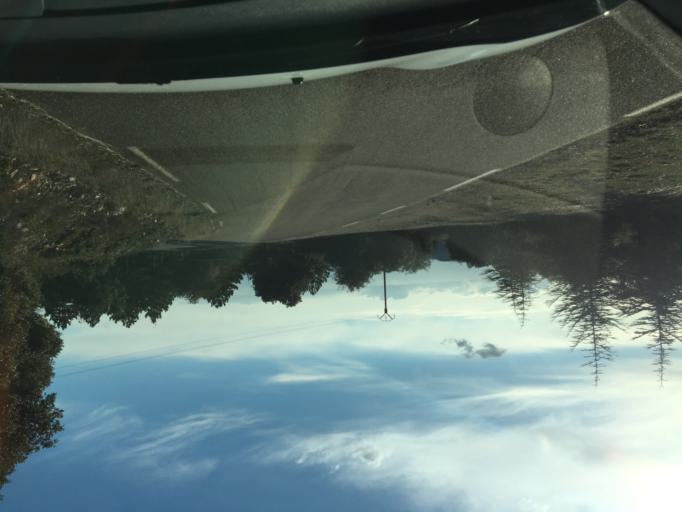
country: FR
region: Provence-Alpes-Cote d'Azur
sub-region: Departement du Vaucluse
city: Villes-sur-Auzon
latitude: 44.0400
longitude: 5.2475
